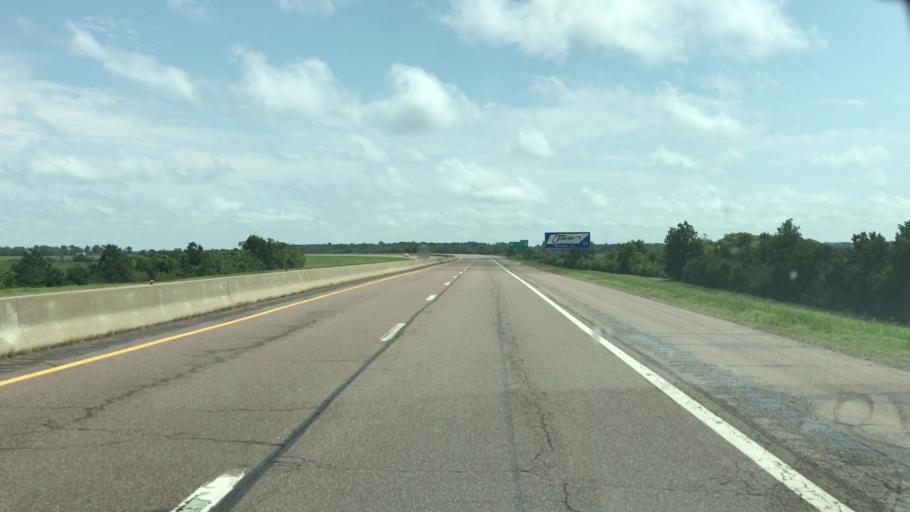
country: US
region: Missouri
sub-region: Pemiscot County
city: Caruthersville
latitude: 36.1027
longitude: -89.6061
